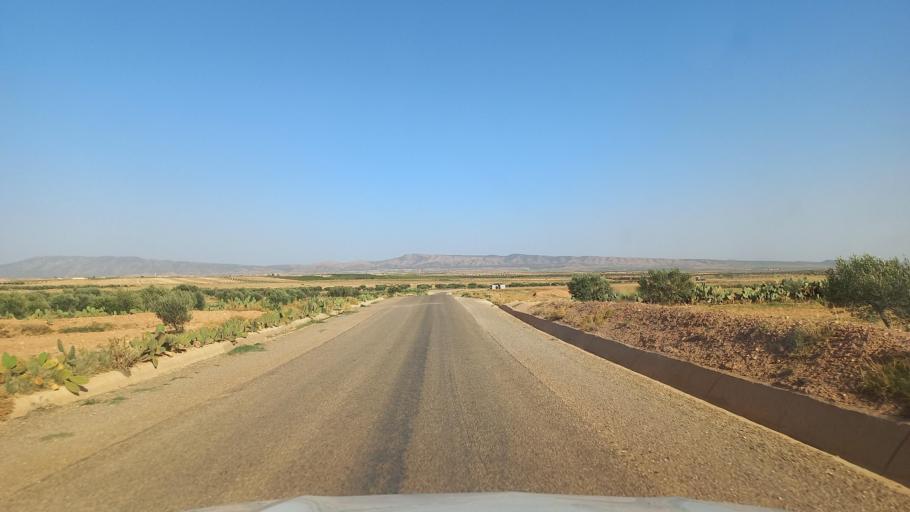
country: TN
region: Al Qasrayn
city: Sbiba
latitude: 35.3782
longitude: 9.0283
